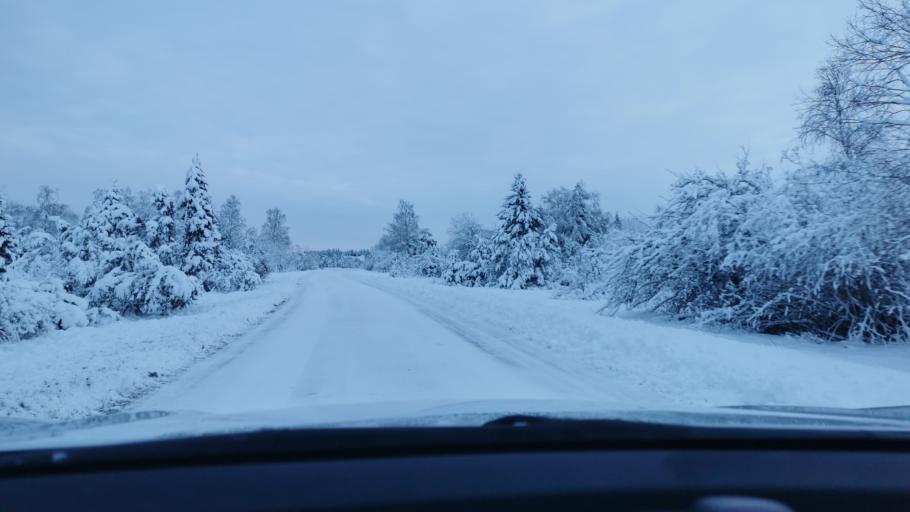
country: EE
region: Laeaene-Virumaa
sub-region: Haljala vald
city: Haljala
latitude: 59.4882
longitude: 26.3765
